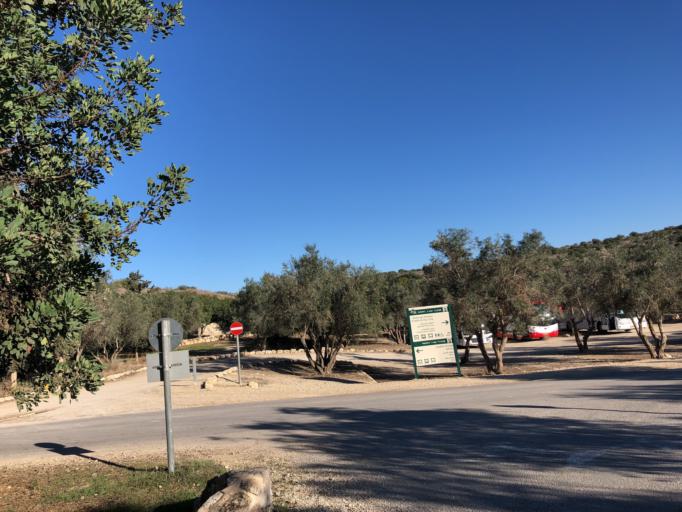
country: PS
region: West Bank
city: Idhna
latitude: 31.5905
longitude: 34.9027
